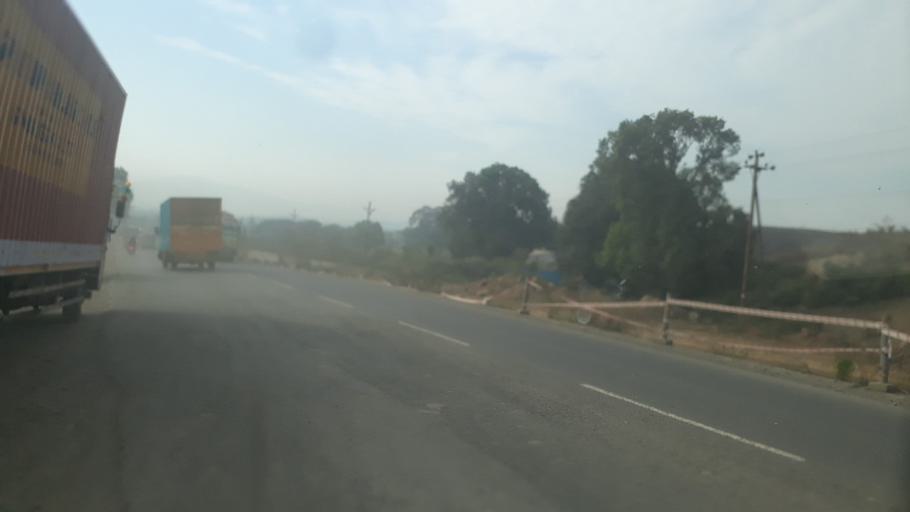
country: IN
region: Maharashtra
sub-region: Raigarh
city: Pen
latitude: 18.7700
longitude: 73.0917
